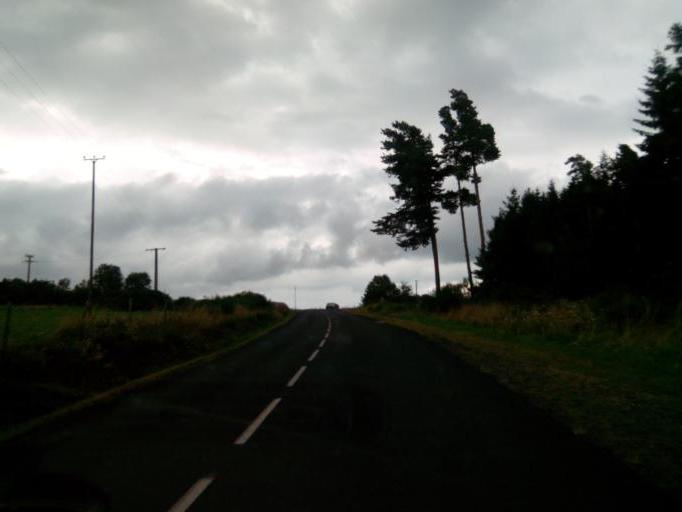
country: FR
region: Rhone-Alpes
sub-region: Departement de la Loire
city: Usson-en-Forez
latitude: 45.3545
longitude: 3.9067
